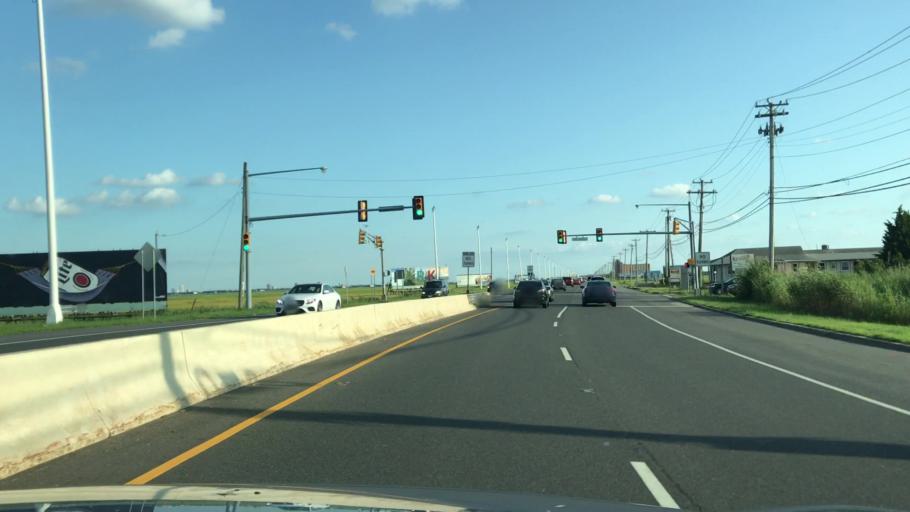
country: US
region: New Jersey
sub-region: Atlantic County
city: Absecon
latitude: 39.4158
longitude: -74.4913
